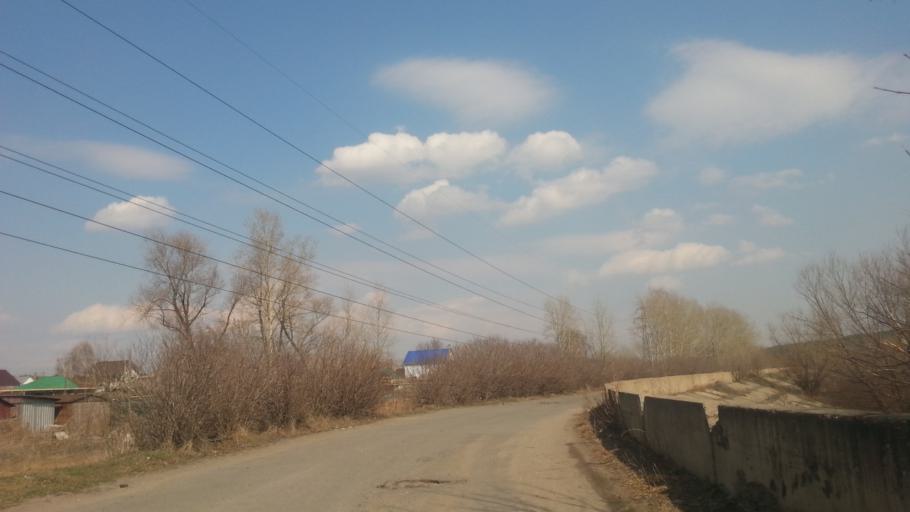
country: RU
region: Altai Krai
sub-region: Gorod Barnaulskiy
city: Barnaul
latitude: 53.3113
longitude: 83.7255
